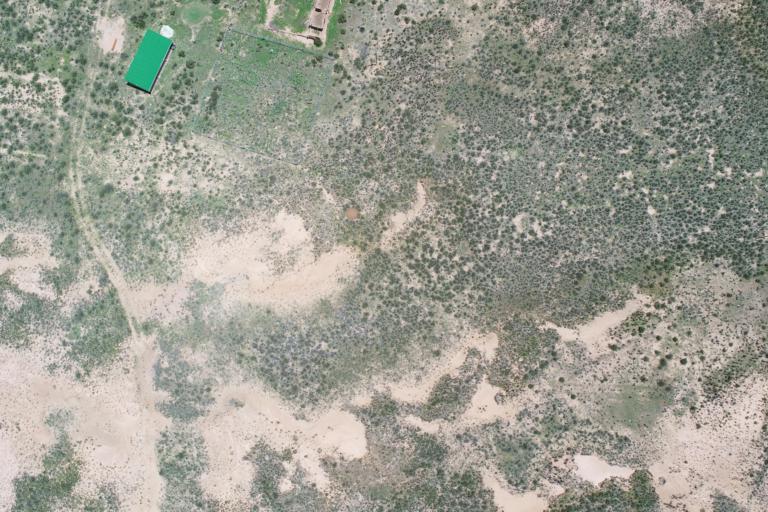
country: BO
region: La Paz
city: Curahuara de Carangas
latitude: -17.3269
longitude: -68.5082
